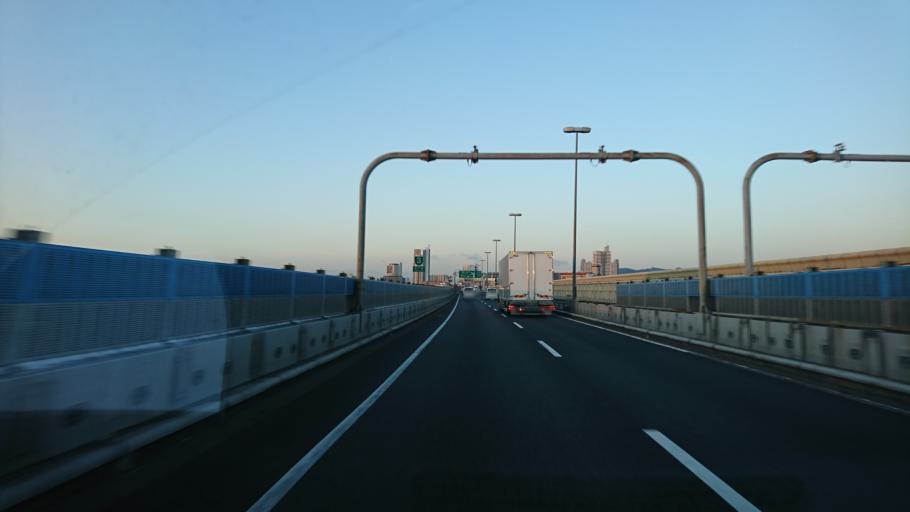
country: JP
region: Hyogo
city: Kobe
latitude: 34.6614
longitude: 135.1582
